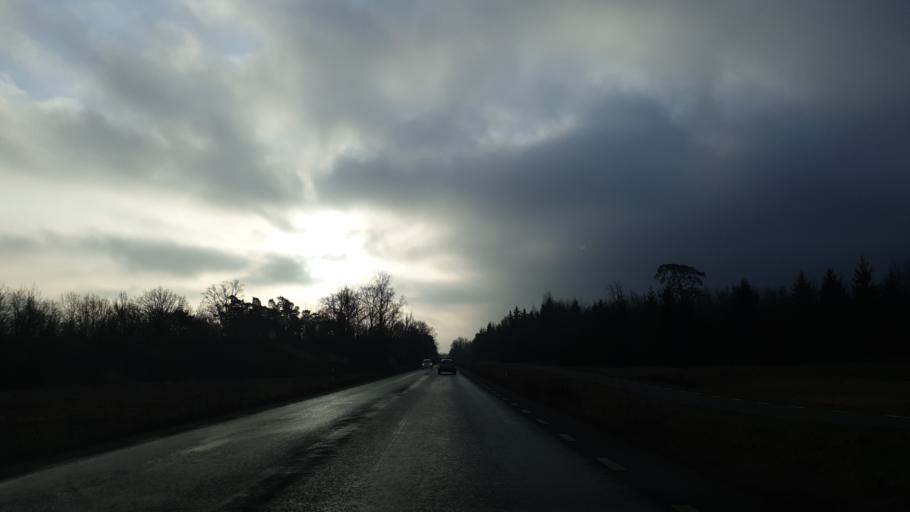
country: SE
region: Blekinge
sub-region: Karlshamns Kommun
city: Morrum
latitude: 56.1436
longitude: 14.6695
